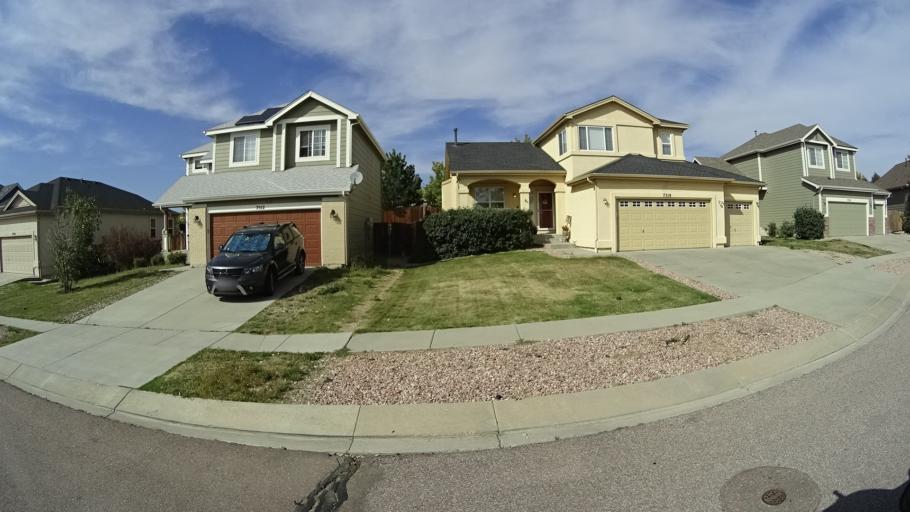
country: US
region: Colorado
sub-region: El Paso County
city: Cimarron Hills
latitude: 38.9111
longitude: -104.6876
